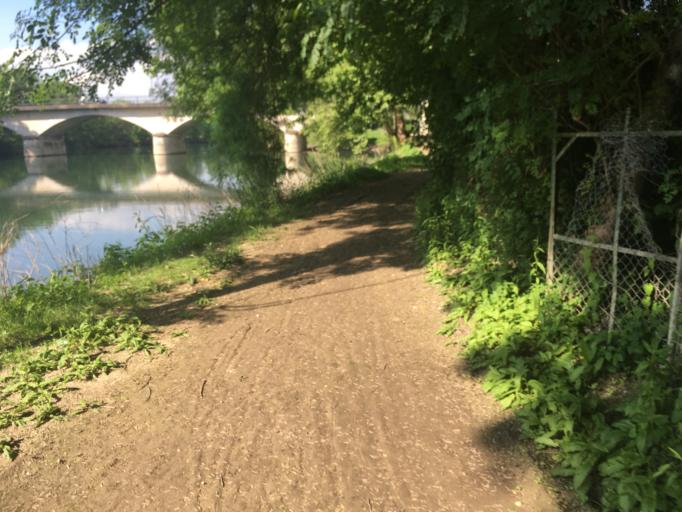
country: FR
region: Poitou-Charentes
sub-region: Departement de la Charente
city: Cognac
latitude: 45.6886
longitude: -0.3395
